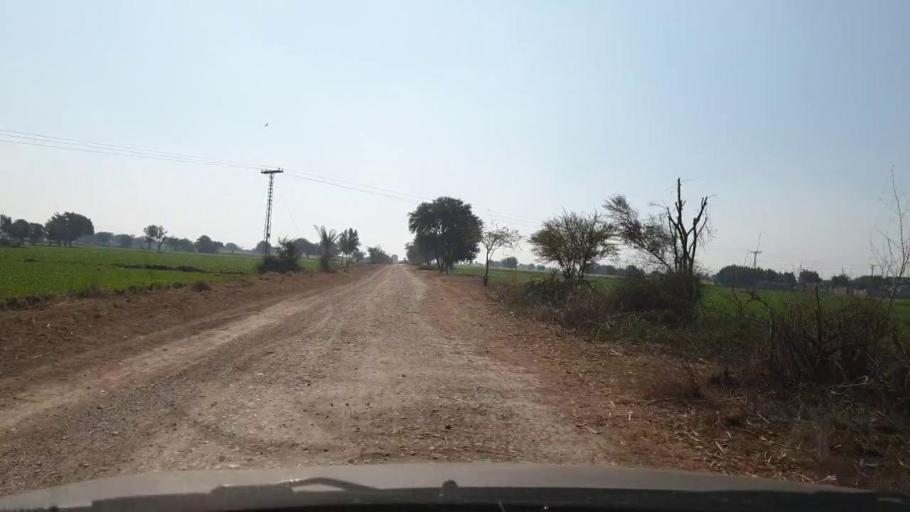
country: PK
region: Sindh
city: Jhol
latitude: 25.9359
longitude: 68.8005
